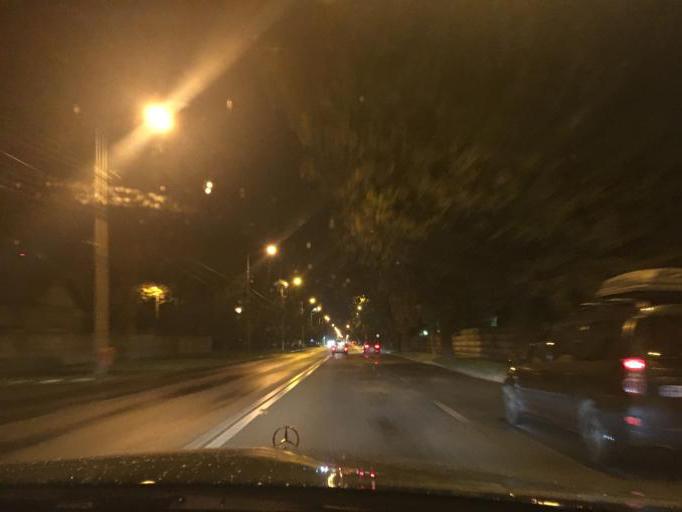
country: RO
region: Bihor
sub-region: Comuna Sanmartin
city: Sanmartin
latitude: 47.0397
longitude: 21.9788
